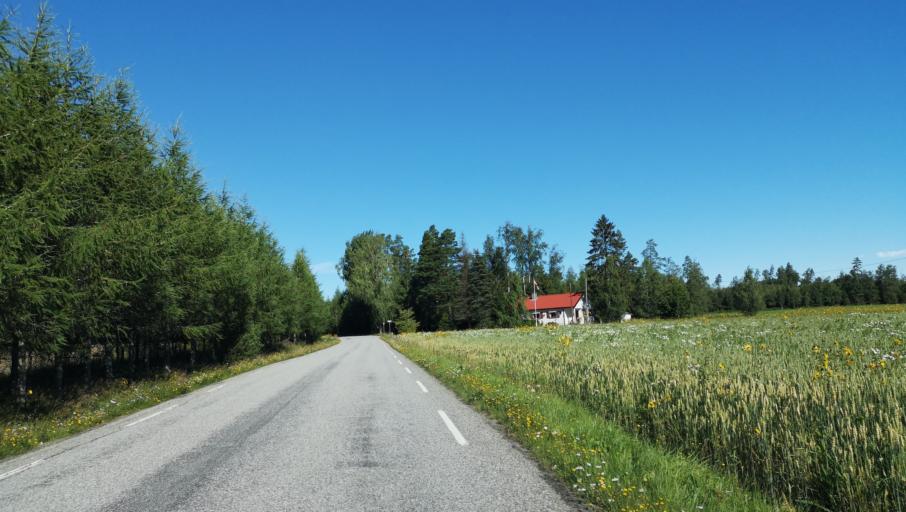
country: NO
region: Ostfold
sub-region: Hobol
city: Knappstad
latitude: 59.6373
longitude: 11.0222
